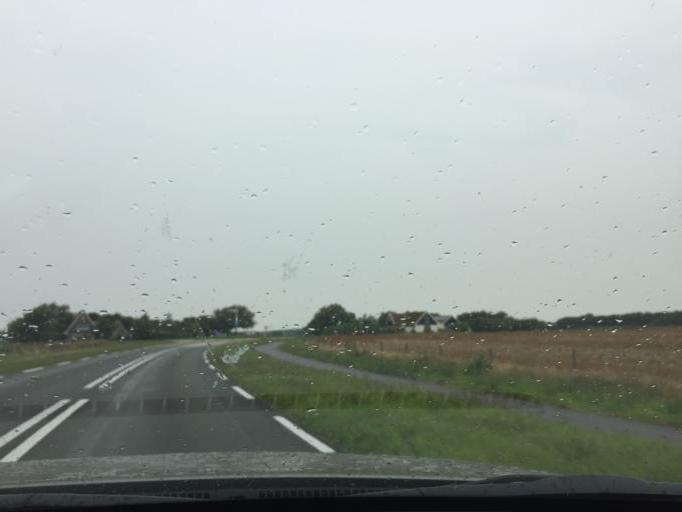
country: NL
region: North Holland
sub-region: Gemeente Texel
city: Den Burg
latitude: 53.0630
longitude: 4.7773
